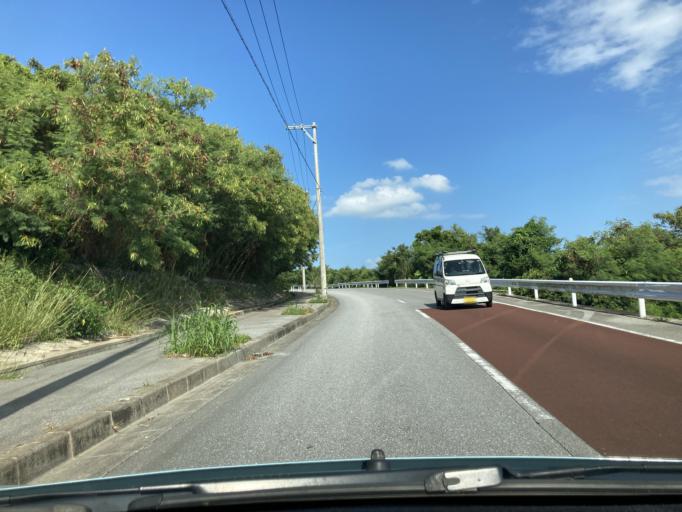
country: JP
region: Okinawa
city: Ginowan
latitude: 26.2782
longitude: 127.7978
